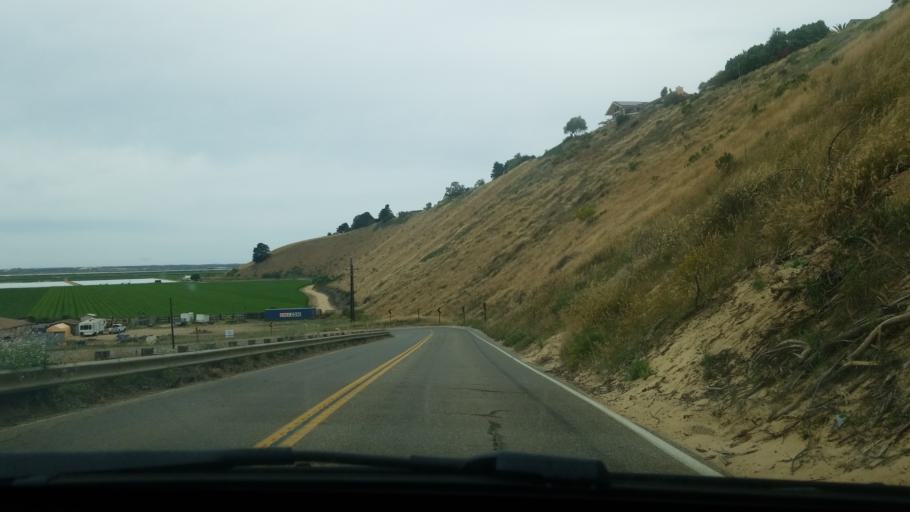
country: US
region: California
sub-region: San Luis Obispo County
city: Nipomo
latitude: 35.0098
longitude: -120.5006
